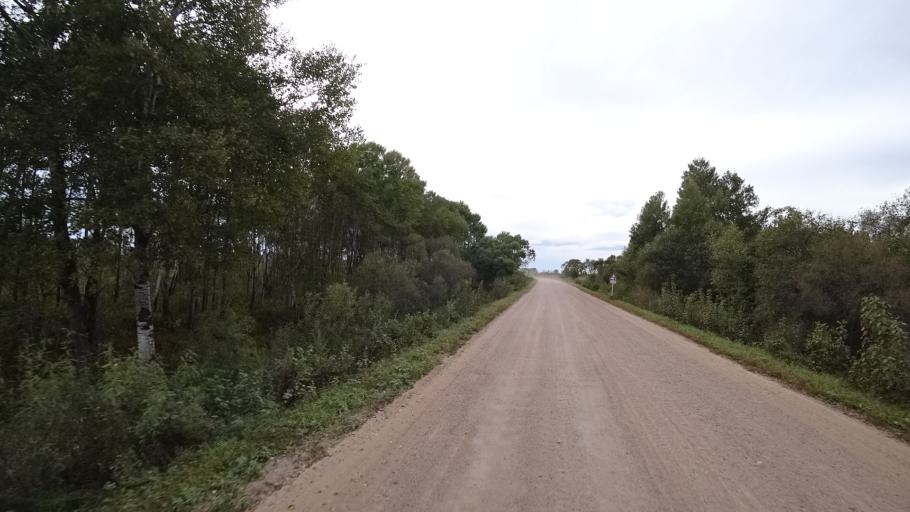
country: RU
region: Amur
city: Arkhara
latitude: 49.3760
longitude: 130.1896
